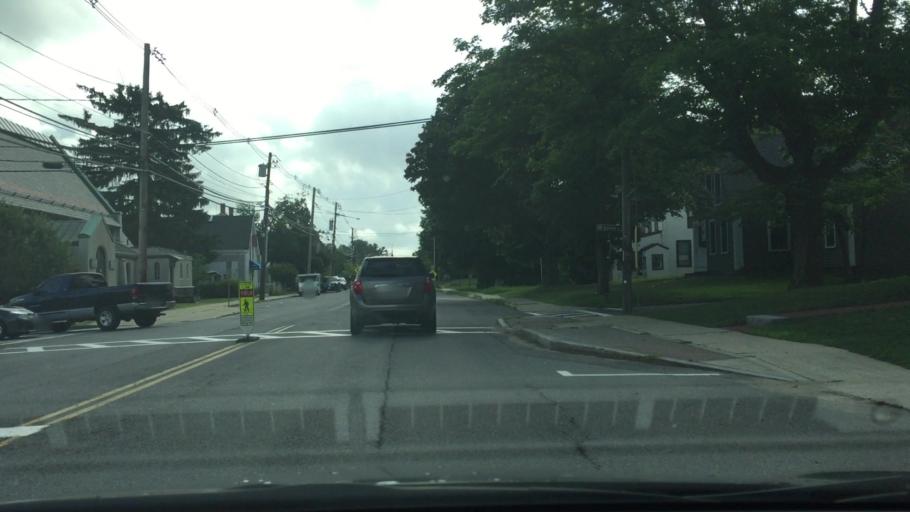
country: US
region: Massachusetts
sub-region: Middlesex County
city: Acton
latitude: 42.4760
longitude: -71.4726
